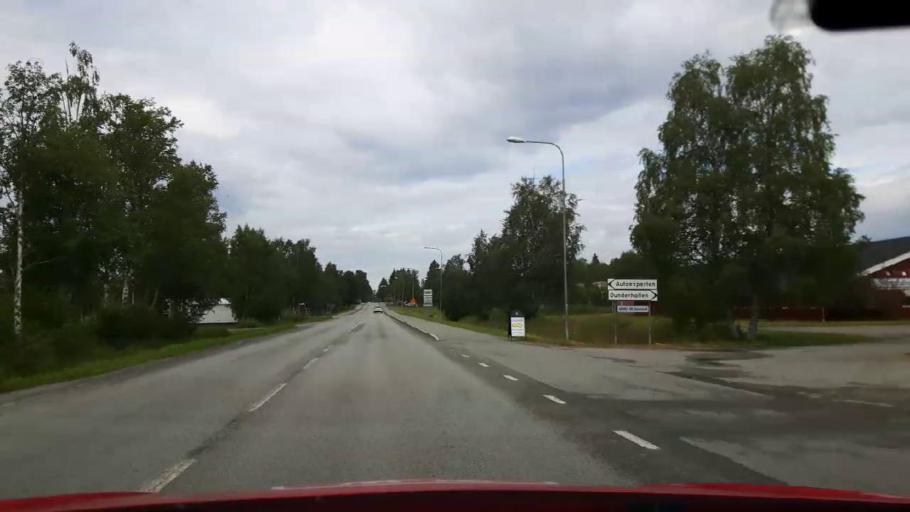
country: SE
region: Jaemtland
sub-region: Stroemsunds Kommun
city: Stroemsund
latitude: 63.8478
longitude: 15.5684
